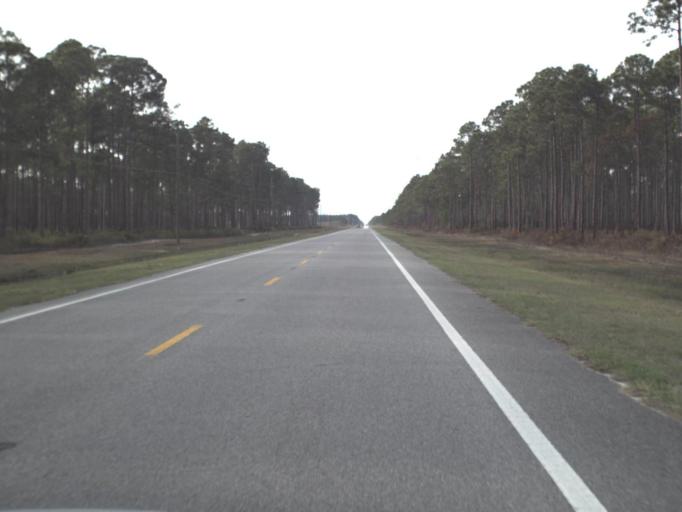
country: US
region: Florida
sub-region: Bay County
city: Tyndall Air Force Base
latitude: 30.0140
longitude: -85.5176
